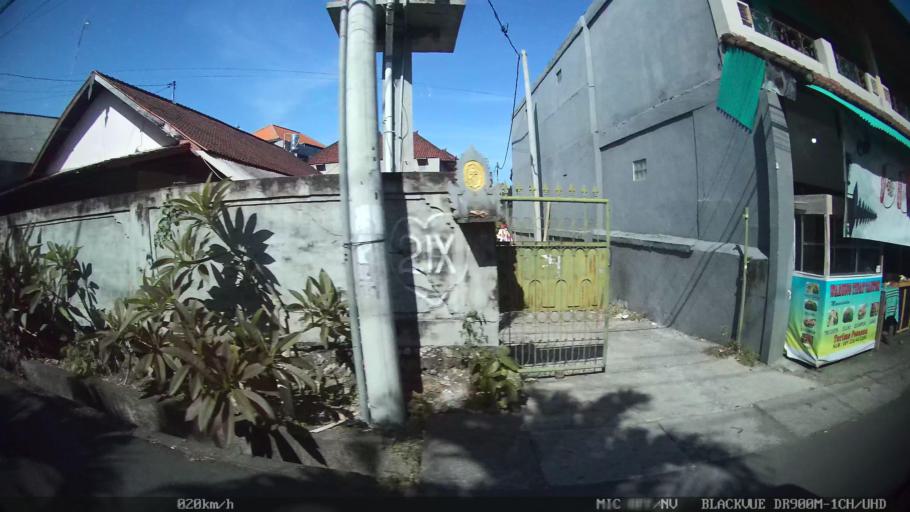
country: ID
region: Bali
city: Denpasar
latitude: -8.6493
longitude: 115.1762
